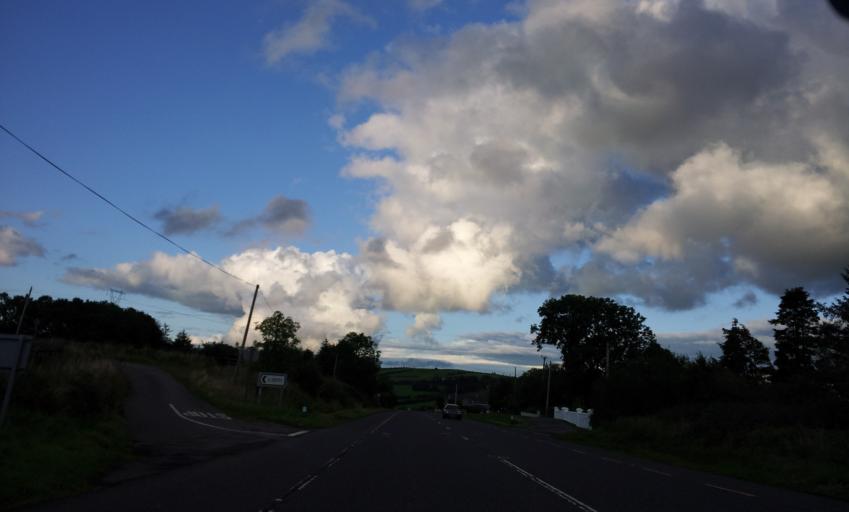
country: IE
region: Munster
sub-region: County Limerick
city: Abbeyfeale
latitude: 52.3084
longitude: -9.3729
